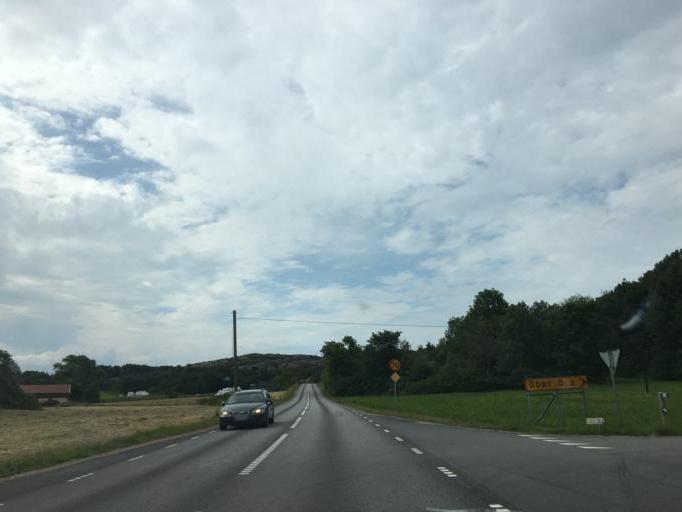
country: SE
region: Vaestra Goetaland
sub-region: Sotenas Kommun
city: Hunnebostrand
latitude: 58.4196
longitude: 11.2896
